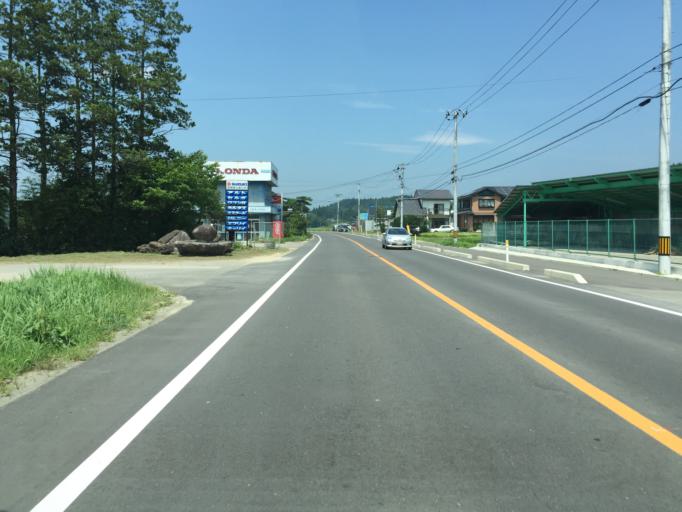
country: JP
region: Miyagi
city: Marumori
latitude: 37.8763
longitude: 140.8231
